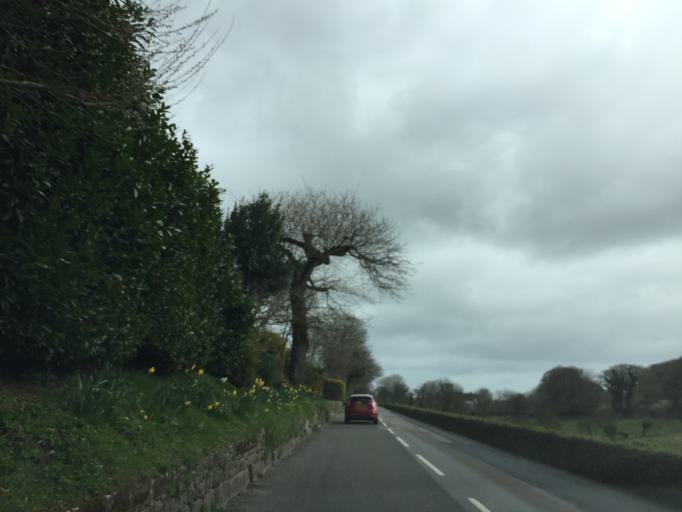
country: JE
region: St Helier
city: Saint Helier
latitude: 49.2275
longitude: -2.1694
